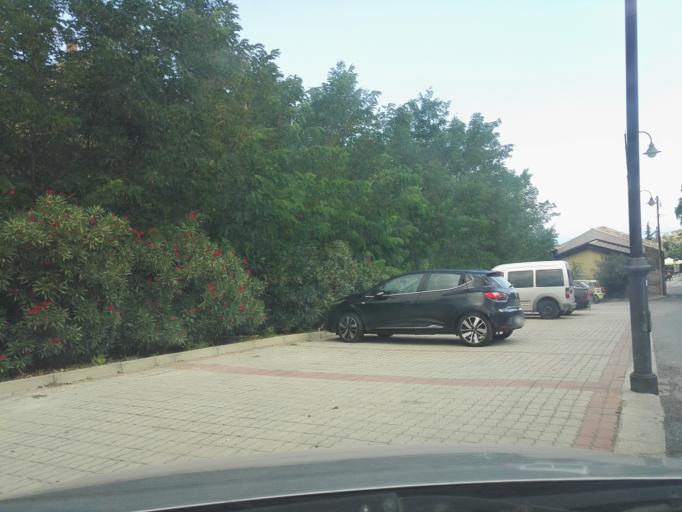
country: IT
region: Calabria
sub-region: Provincia di Reggio Calabria
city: Riace
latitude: 38.4192
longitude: 16.4807
